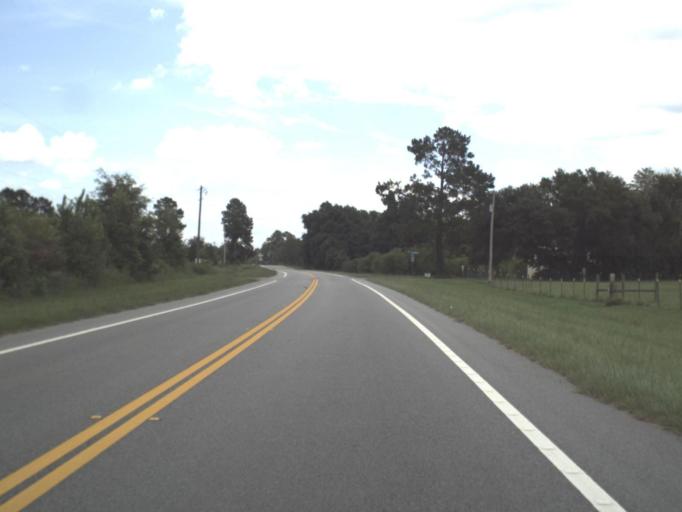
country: US
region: Florida
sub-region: Madison County
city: Madison
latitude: 30.6126
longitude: -83.3361
